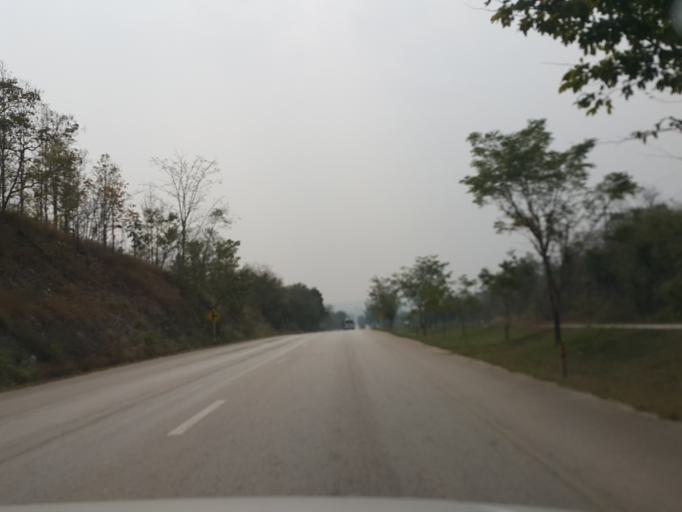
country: TH
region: Lampang
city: Ko Kha
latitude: 18.0954
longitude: 99.3977
